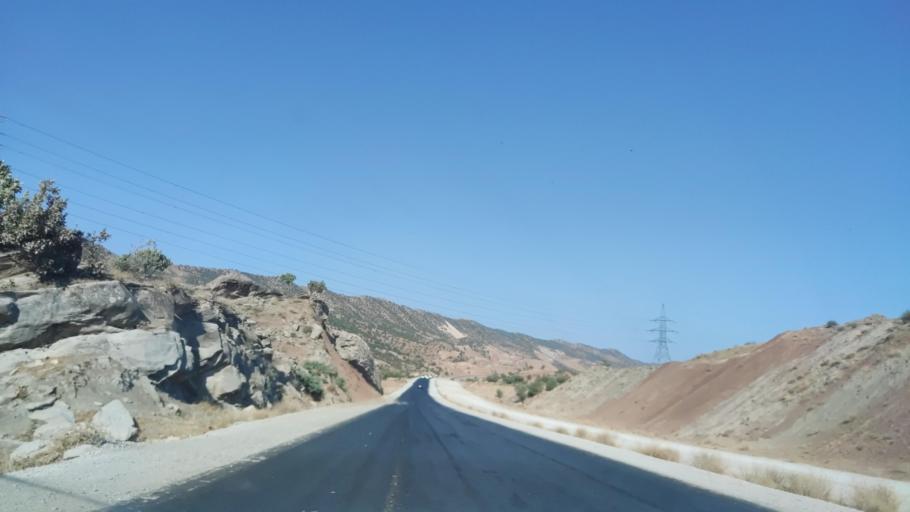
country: IQ
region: Arbil
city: Shaqlawah
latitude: 36.4299
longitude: 44.3311
